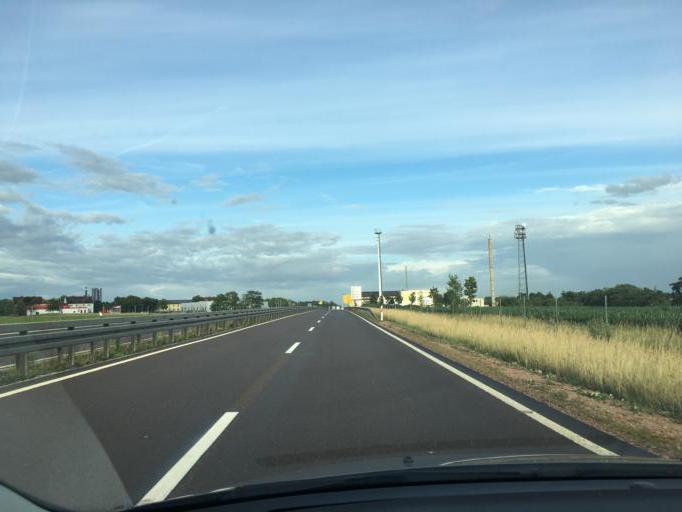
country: DE
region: Saxony-Anhalt
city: Bernburg
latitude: 51.8095
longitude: 11.7184
